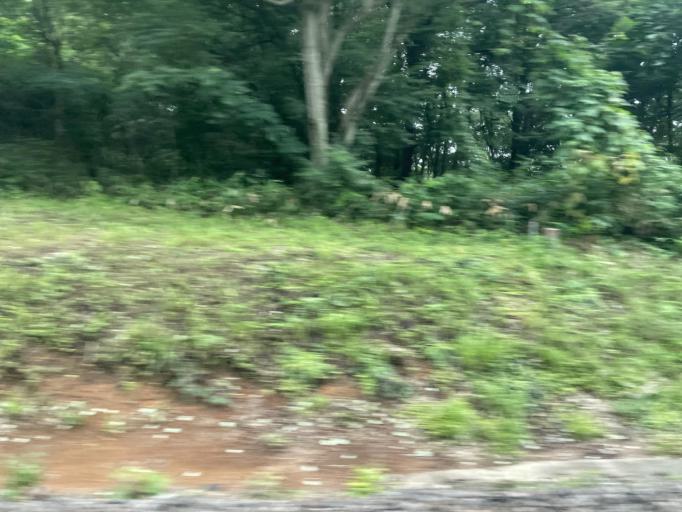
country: JP
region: Tochigi
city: Kuroiso
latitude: 36.9893
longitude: 140.0812
